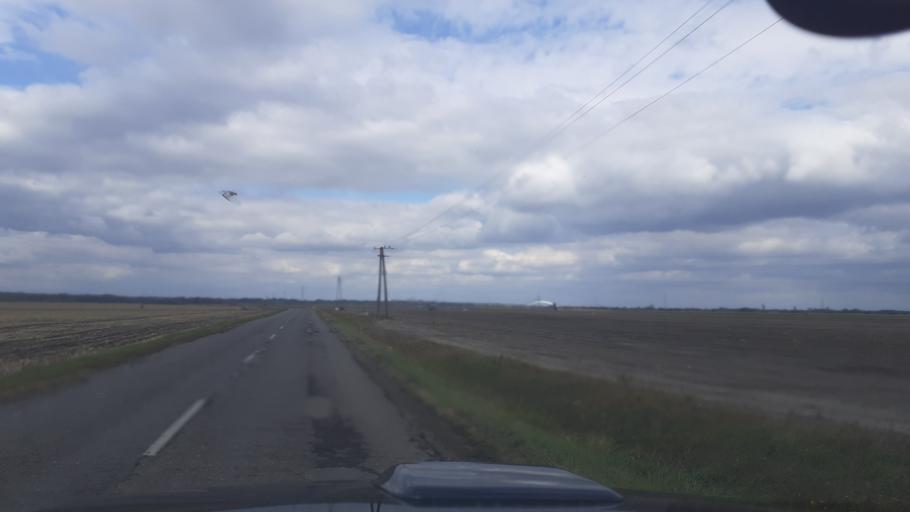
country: HU
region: Bacs-Kiskun
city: Apostag
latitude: 46.8445
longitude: 18.9500
